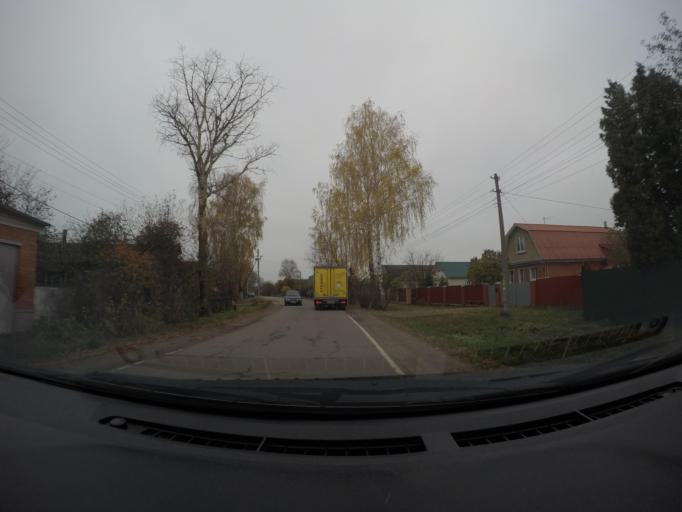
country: RU
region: Moskovskaya
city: Rechitsy
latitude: 55.5848
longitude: 38.5157
